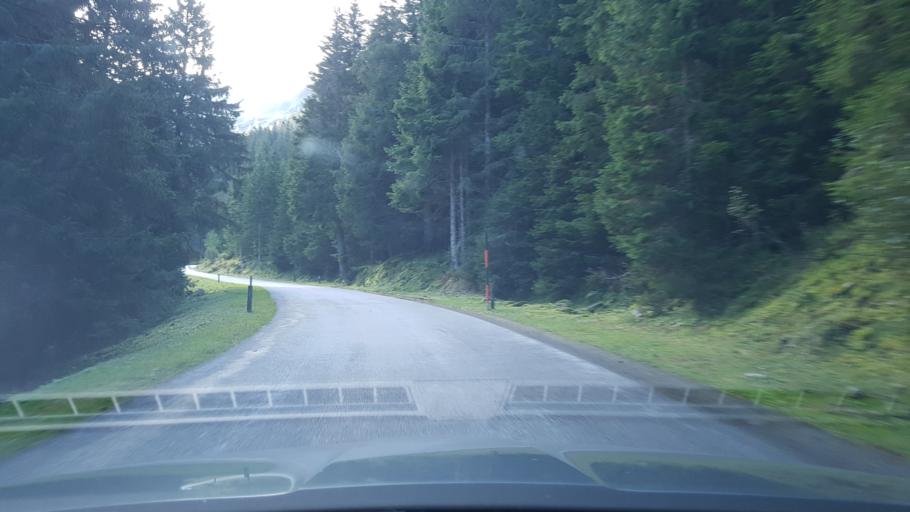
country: AT
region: Styria
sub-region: Politischer Bezirk Liezen
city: Sankt Nikolai im Solktal
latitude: 47.2814
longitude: 14.0858
